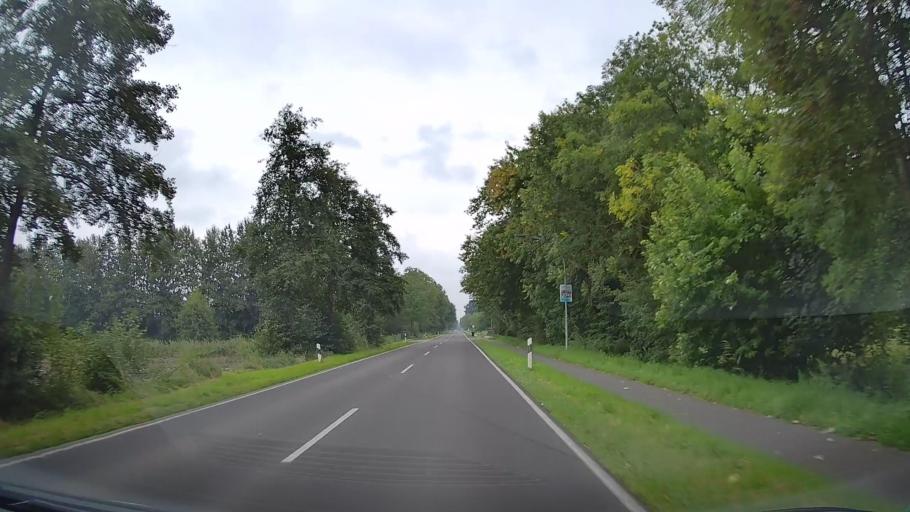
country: DE
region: Lower Saxony
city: Drochtersen
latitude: 53.7285
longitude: 9.3539
